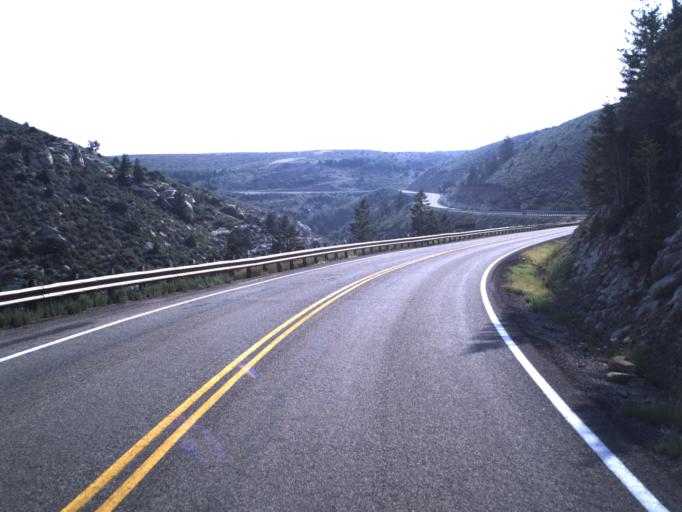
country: US
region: Utah
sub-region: Uintah County
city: Maeser
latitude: 40.6594
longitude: -109.4875
